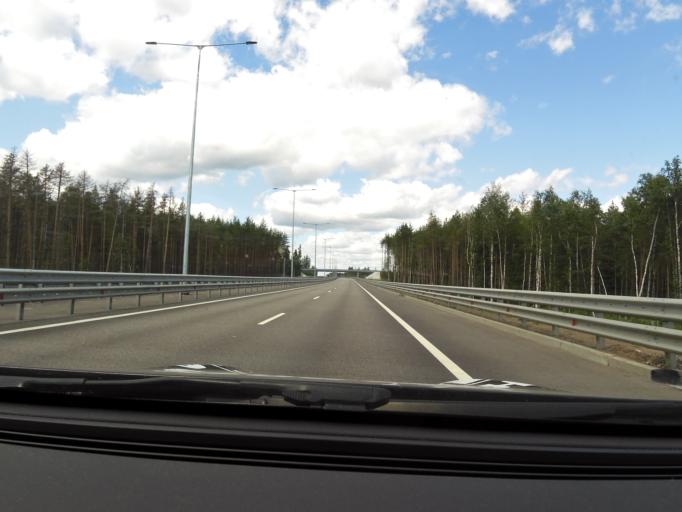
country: RU
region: Tverskaya
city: Vyshniy Volochek
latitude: 57.4197
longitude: 34.5012
